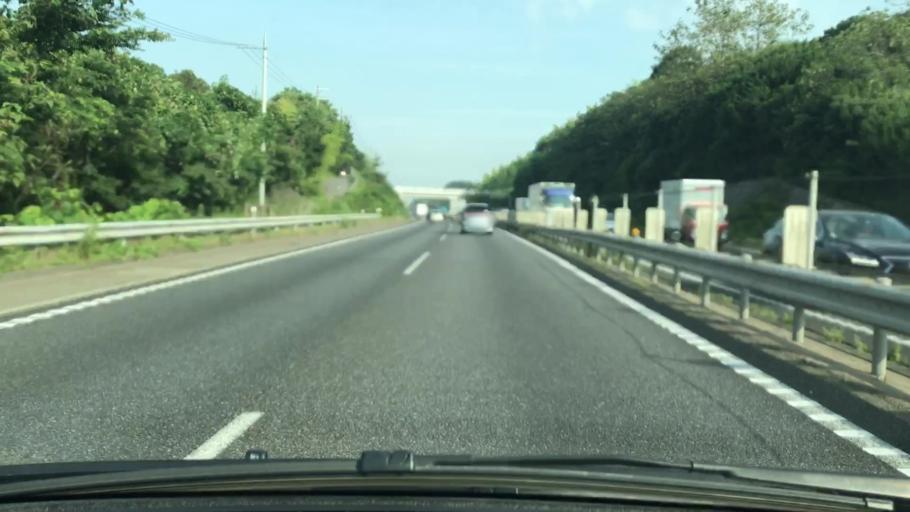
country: JP
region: Hyogo
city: Akashi
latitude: 34.6998
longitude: 134.9644
